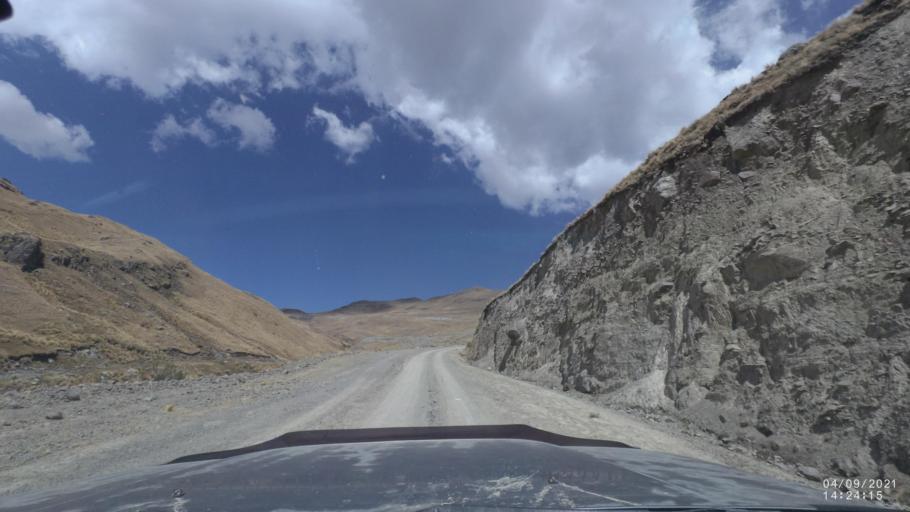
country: BO
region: Cochabamba
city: Sipe Sipe
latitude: -17.2393
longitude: -66.4108
